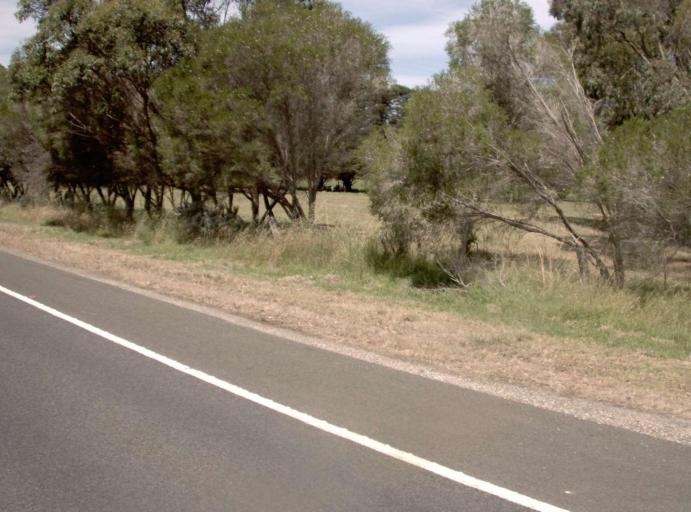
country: AU
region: Victoria
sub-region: Wellington
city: Heyfield
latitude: -38.1133
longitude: 146.8792
